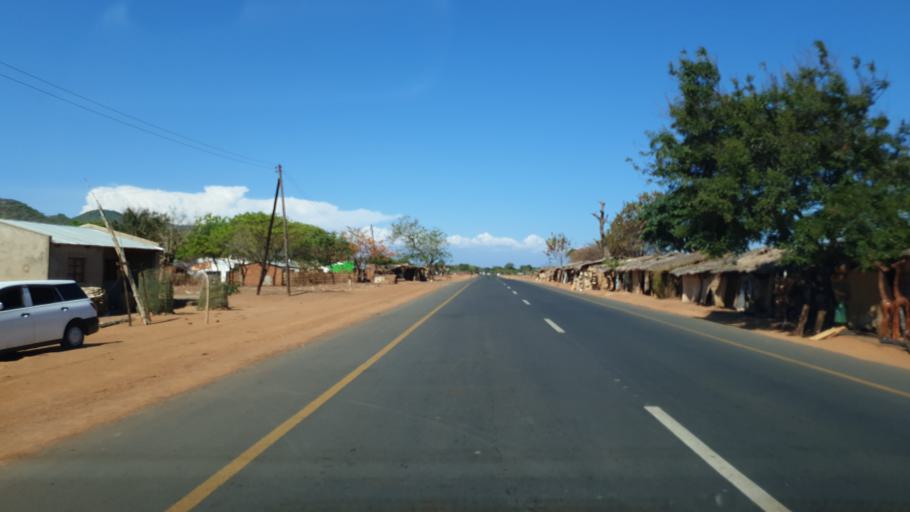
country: MW
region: Central Region
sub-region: Salima District
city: Salima
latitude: -13.7547
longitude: 34.5804
